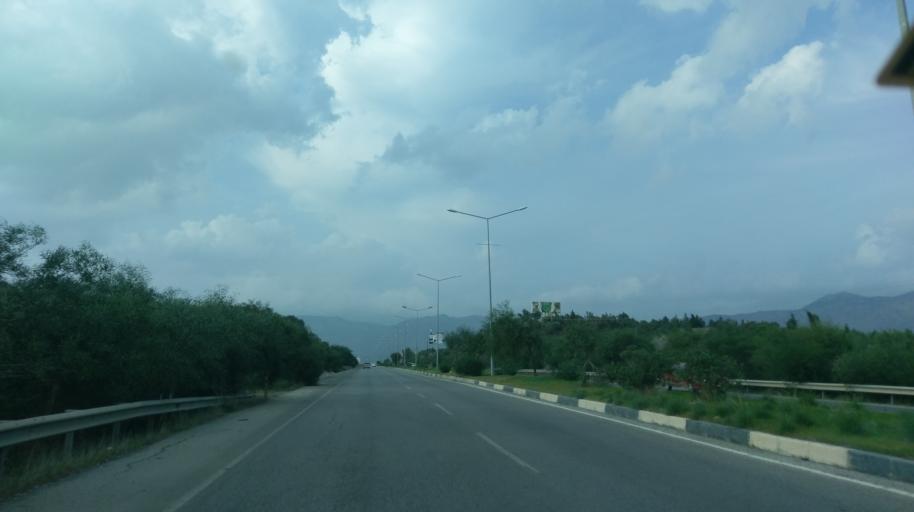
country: CY
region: Keryneia
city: Kyrenia
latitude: 35.2480
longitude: 33.3054
